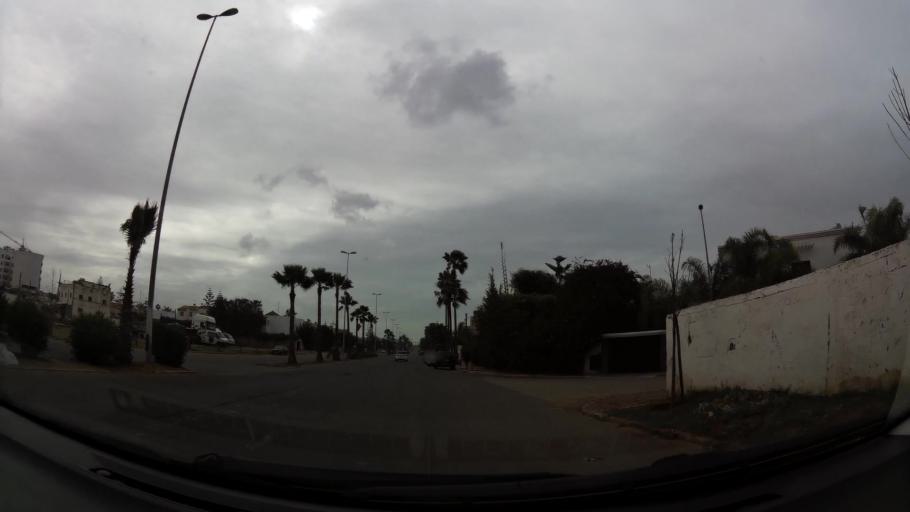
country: MA
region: Grand Casablanca
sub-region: Casablanca
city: Casablanca
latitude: 33.5985
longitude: -7.6502
